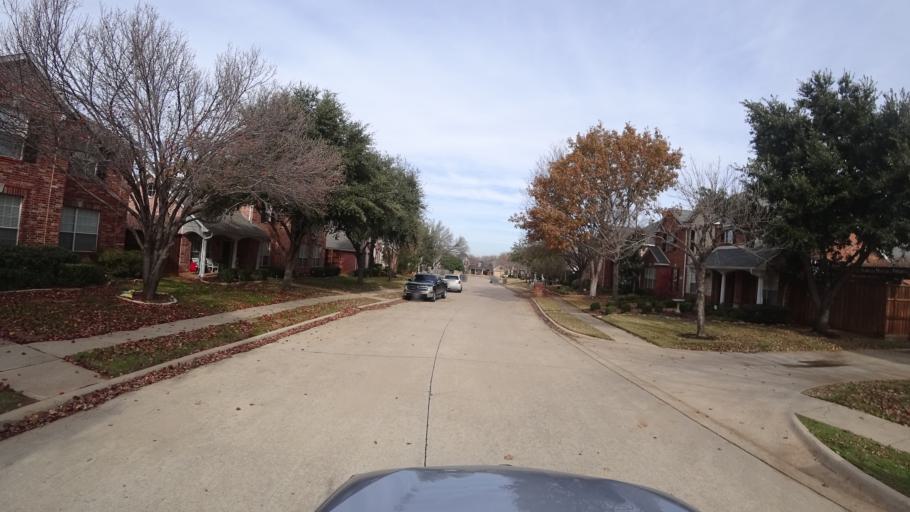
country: US
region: Texas
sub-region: Denton County
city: Highland Village
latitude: 33.0843
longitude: -97.0295
